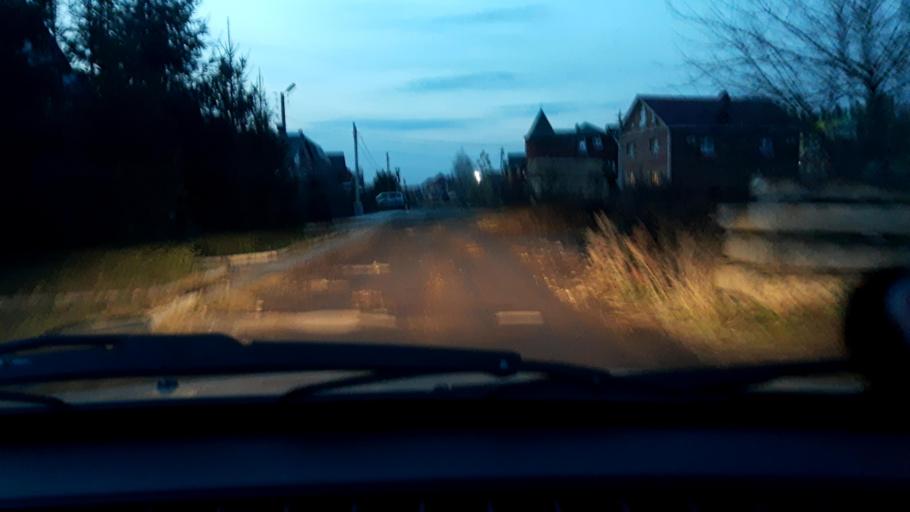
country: RU
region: Bashkortostan
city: Ufa
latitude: 54.7938
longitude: 55.9517
